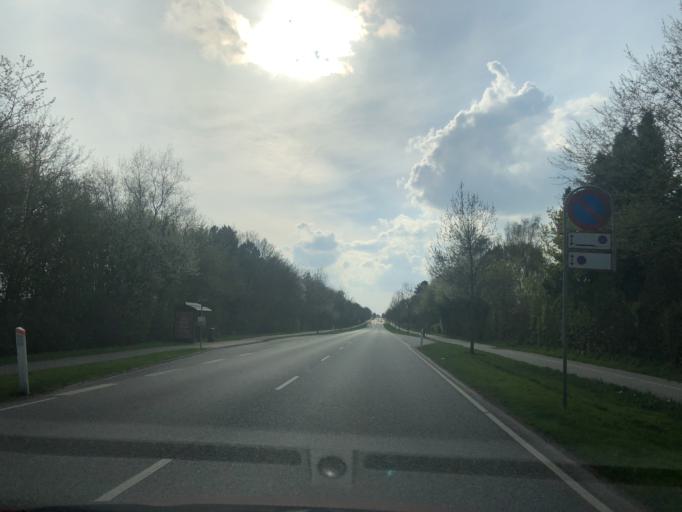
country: DK
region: Zealand
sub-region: Ringsted Kommune
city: Ringsted
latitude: 55.4444
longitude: 11.8210
